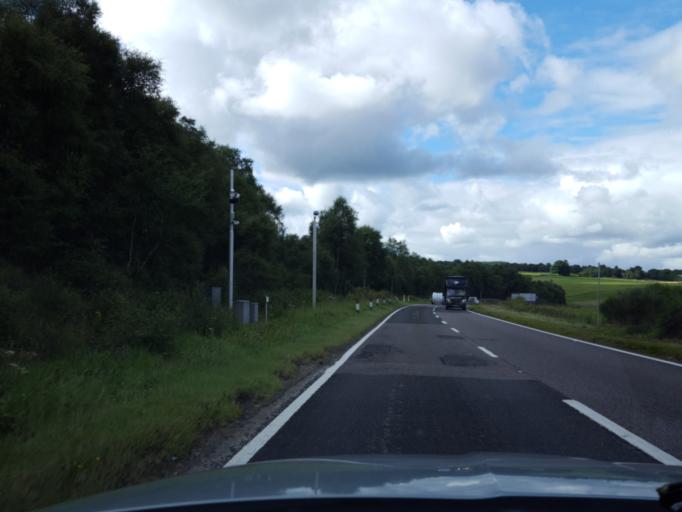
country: GB
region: Scotland
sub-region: Highland
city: Grantown on Spey
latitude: 57.3219
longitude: -3.5594
